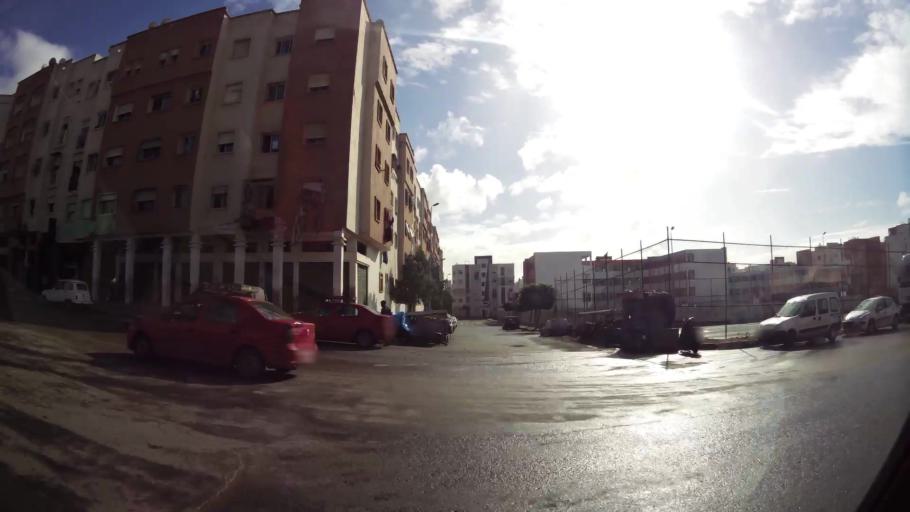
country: MA
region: Grand Casablanca
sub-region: Casablanca
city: Casablanca
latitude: 33.5547
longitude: -7.7012
